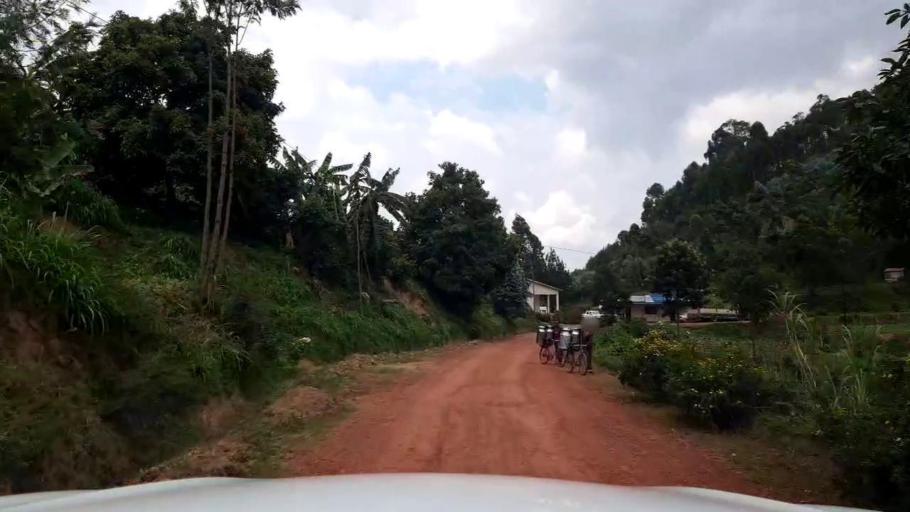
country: RW
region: Northern Province
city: Byumba
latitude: -1.4835
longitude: 29.9187
